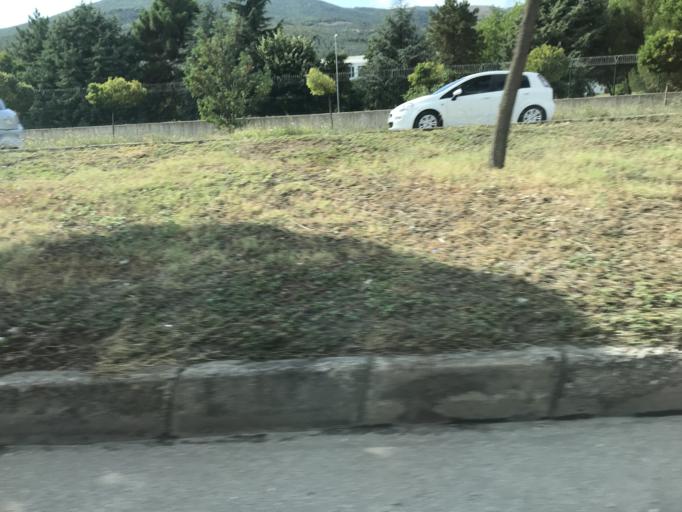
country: TR
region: Bursa
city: Orhangazi
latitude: 40.4541
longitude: 29.2857
